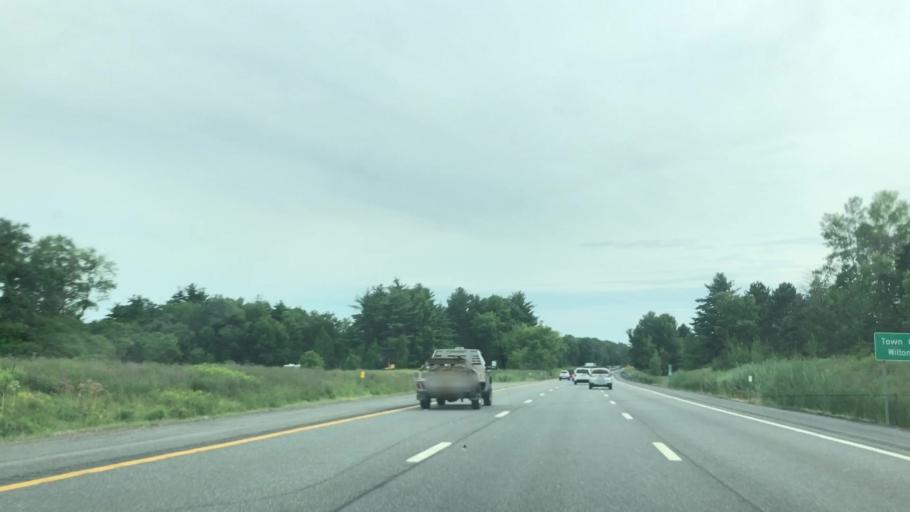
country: US
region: New York
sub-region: Warren County
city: West Glens Falls
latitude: 43.2054
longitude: -73.6961
